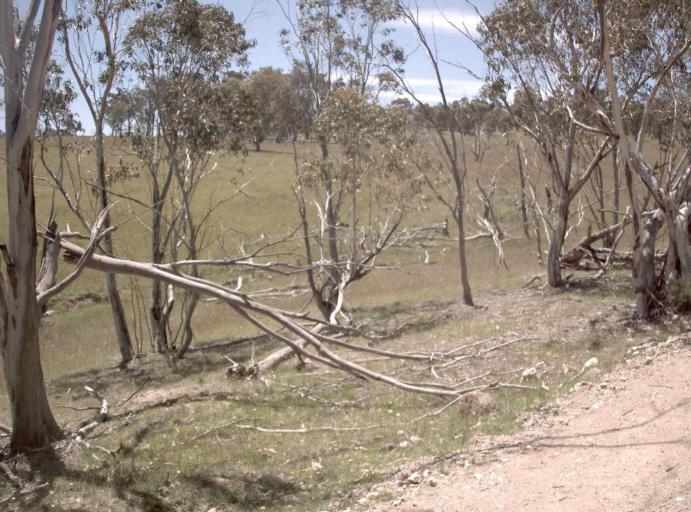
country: AU
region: New South Wales
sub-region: Snowy River
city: Jindabyne
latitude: -37.0601
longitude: 148.2991
